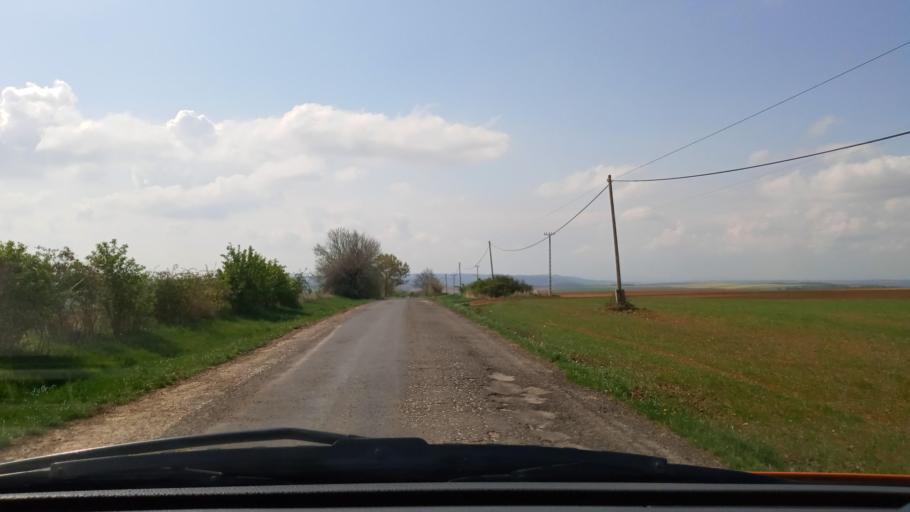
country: HU
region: Baranya
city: Pecsvarad
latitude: 46.1062
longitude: 18.4961
